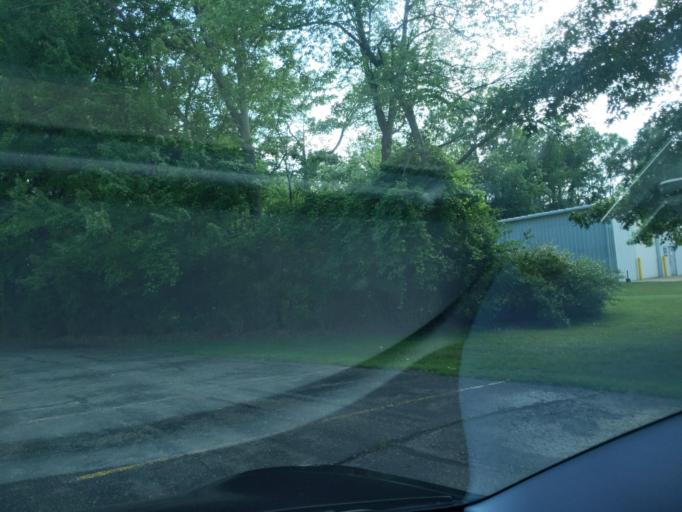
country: US
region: Michigan
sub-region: Jackson County
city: Jackson
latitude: 42.2295
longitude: -84.3711
